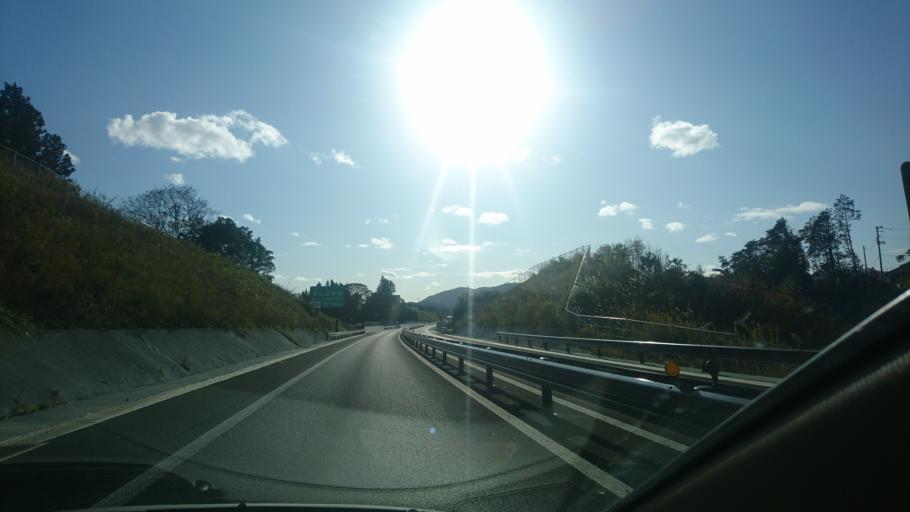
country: JP
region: Iwate
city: Ofunato
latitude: 38.8765
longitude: 141.5838
